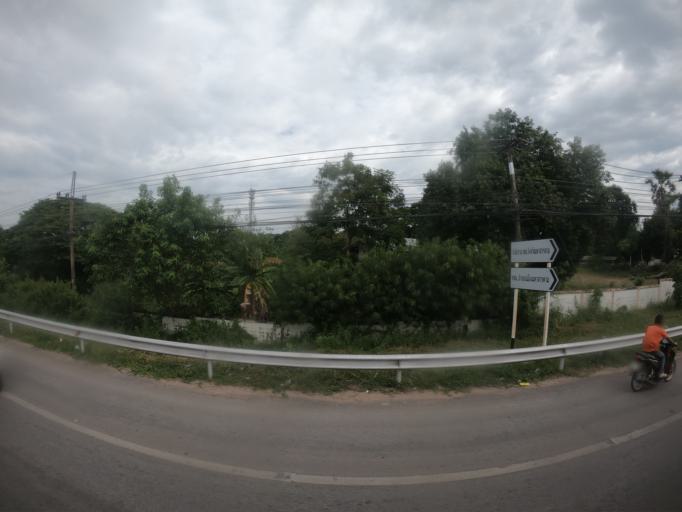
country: TH
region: Maha Sarakham
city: Maha Sarakham
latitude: 16.2040
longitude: 103.2875
